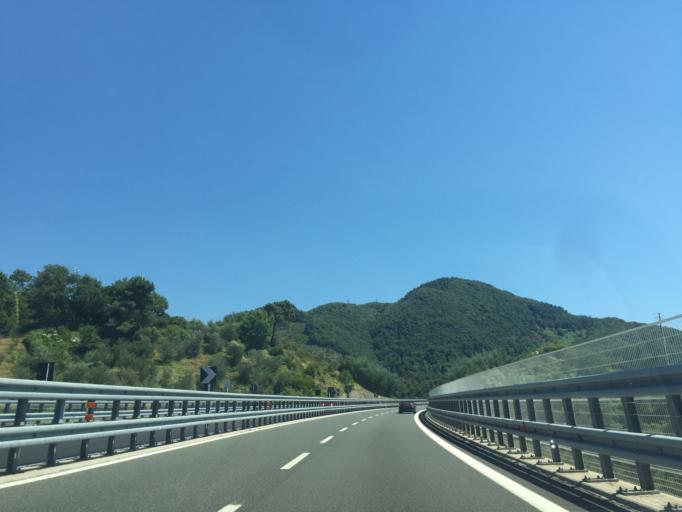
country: IT
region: Tuscany
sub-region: Provincia di Lucca
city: Massarosa
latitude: 43.8698
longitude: 10.3626
